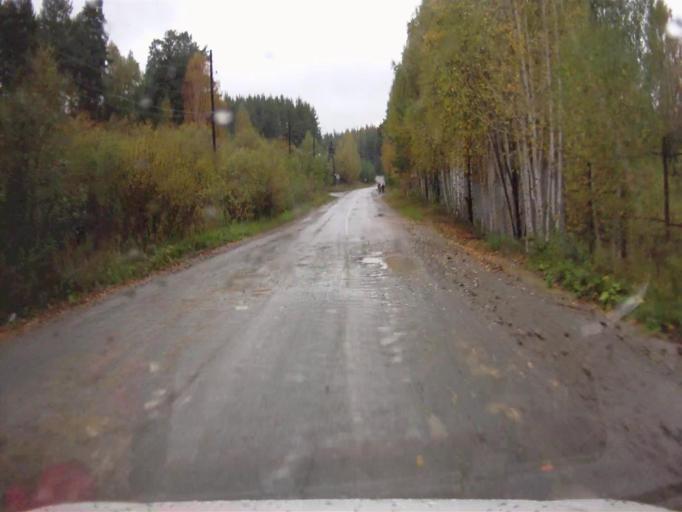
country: RU
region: Chelyabinsk
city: Kyshtym
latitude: 55.7444
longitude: 60.4924
